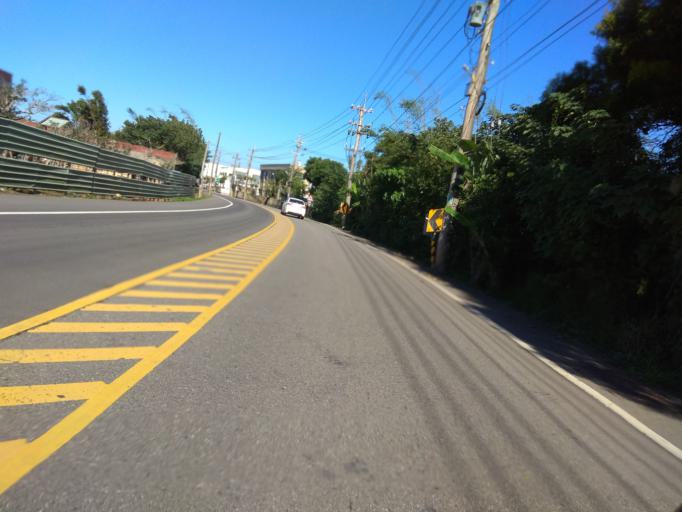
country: TW
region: Taiwan
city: Taoyuan City
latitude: 24.9872
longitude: 121.1345
